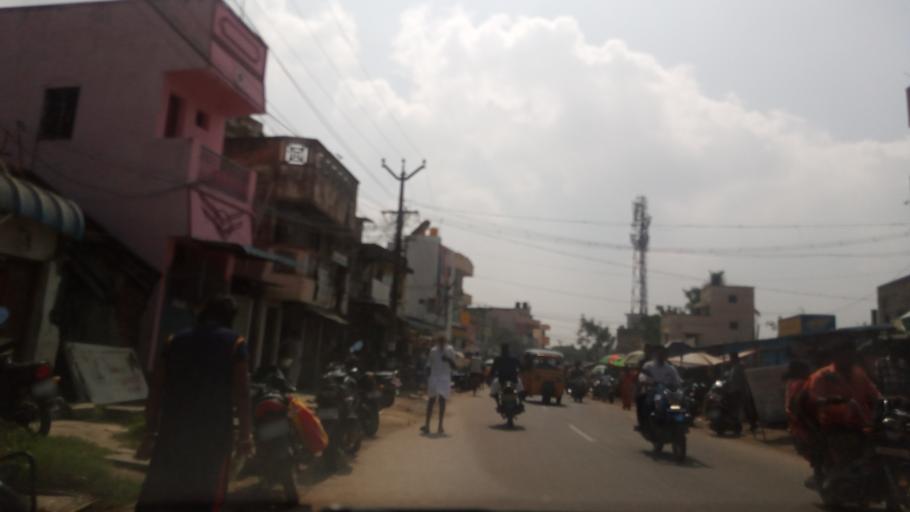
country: IN
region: Tamil Nadu
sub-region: Vellore
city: Arakkonam
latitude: 13.0797
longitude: 79.6715
